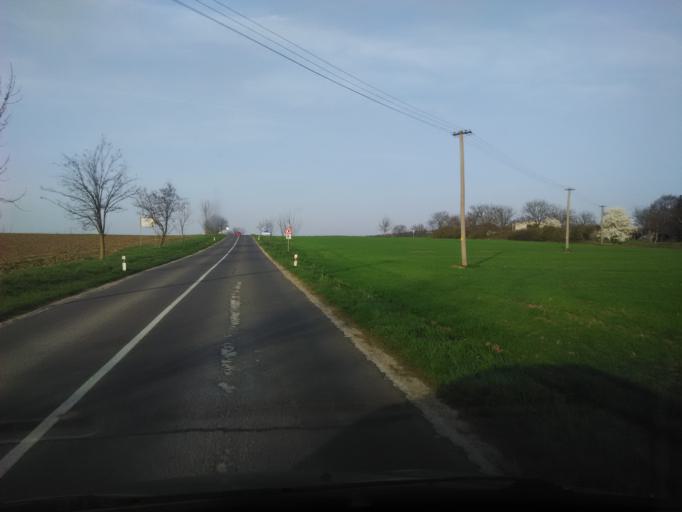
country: SK
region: Nitriansky
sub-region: Okres Nitra
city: Vrable
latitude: 48.1184
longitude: 18.3804
